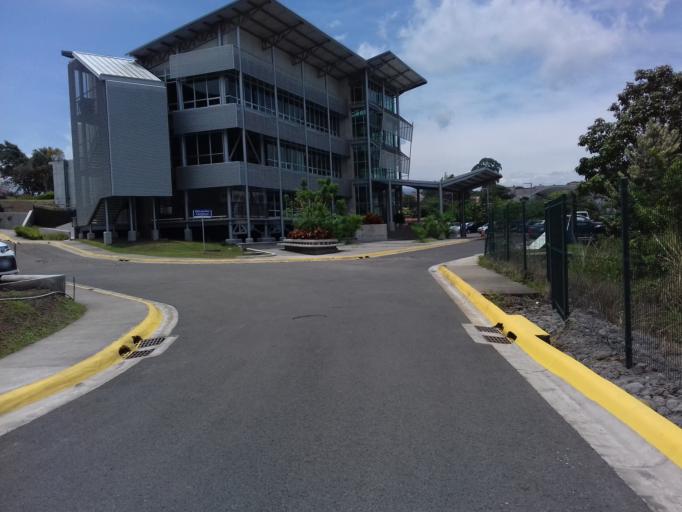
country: CR
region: San Jose
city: San Pedro
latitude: 9.9357
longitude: -84.0442
